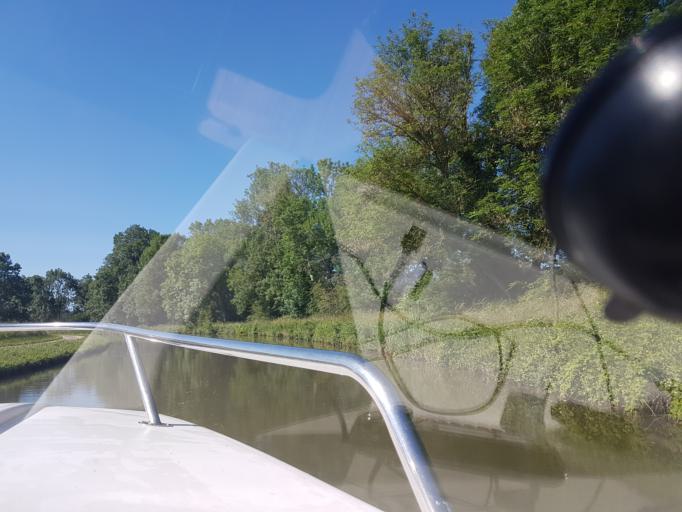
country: FR
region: Bourgogne
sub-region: Departement de la Nievre
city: Clamecy
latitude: 47.5360
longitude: 3.5998
